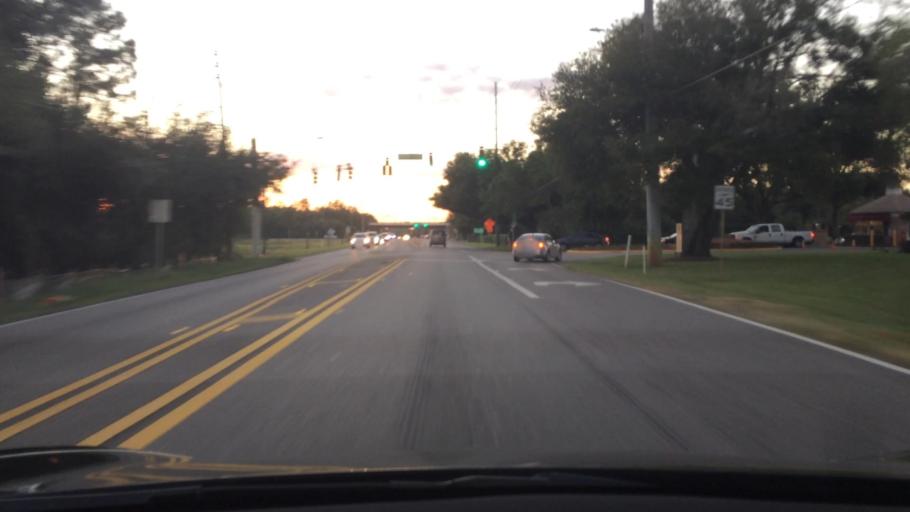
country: US
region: Florida
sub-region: Hillsborough County
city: Greater Northdale
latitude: 28.1283
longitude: -82.5436
